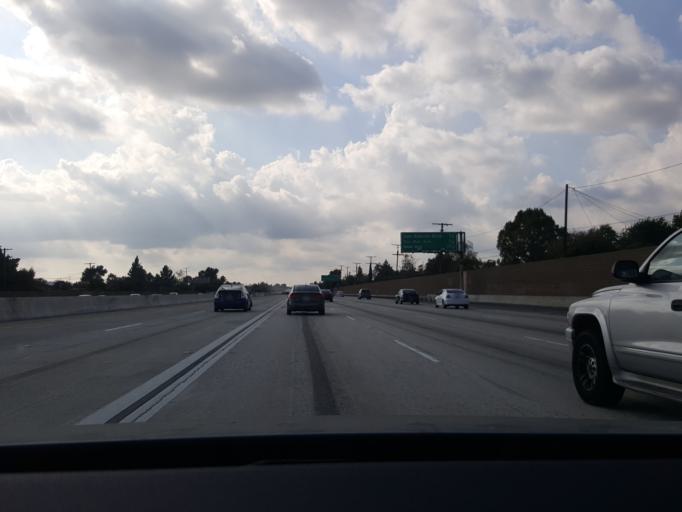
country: US
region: California
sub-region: Los Angeles County
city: South San Gabriel
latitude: 34.0722
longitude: -118.0846
